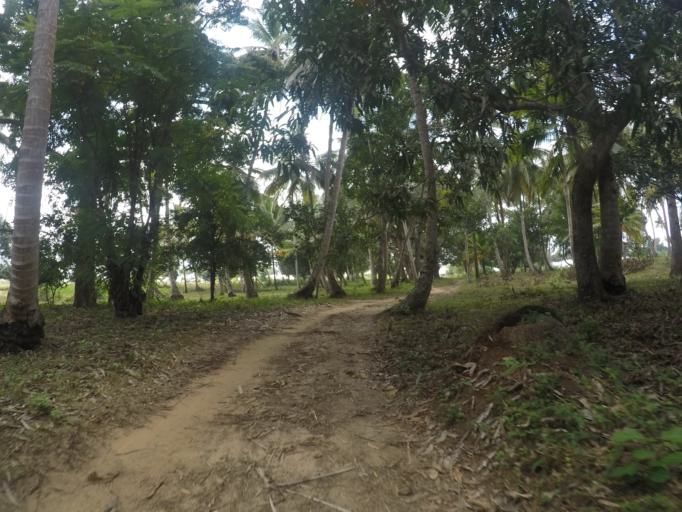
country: TZ
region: Zanzibar Urban/West
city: Zanzibar
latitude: -6.2055
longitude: 39.2384
